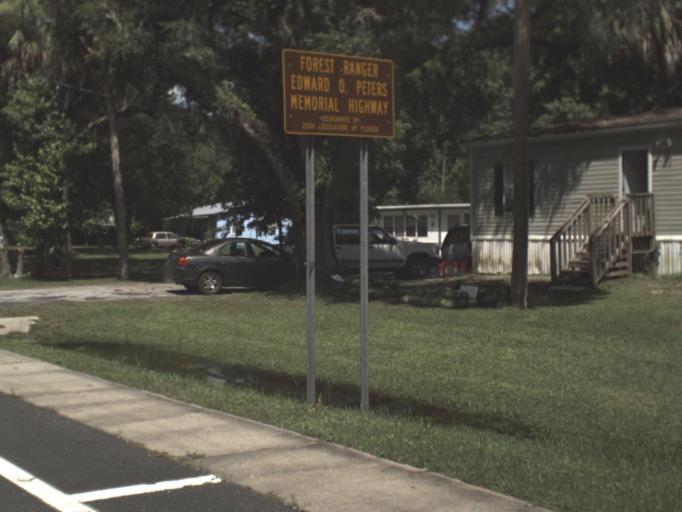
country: US
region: Florida
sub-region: Levy County
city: Chiefland
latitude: 29.3263
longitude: -82.7707
